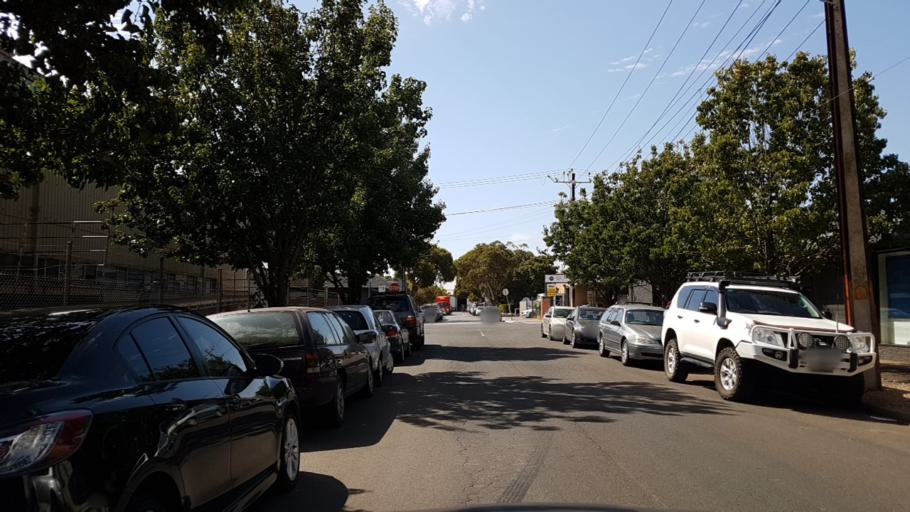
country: AU
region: South Australia
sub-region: Marion
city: Clovelly Park
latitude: -34.9912
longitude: 138.5776
